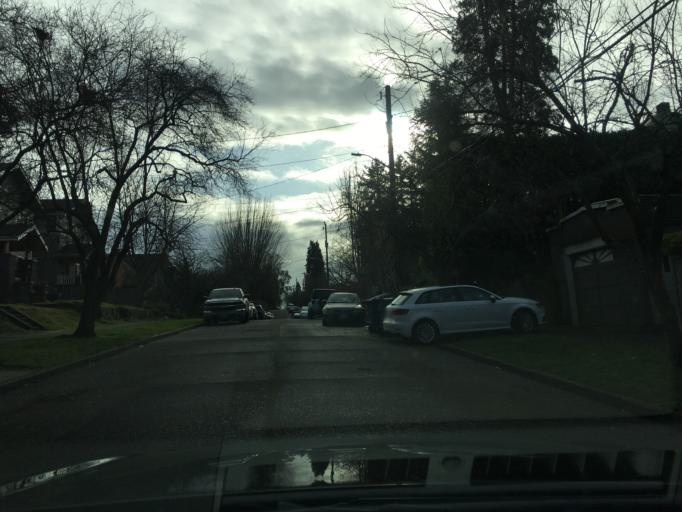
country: US
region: Washington
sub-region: King County
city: Seattle
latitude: 47.6717
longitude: -122.3350
